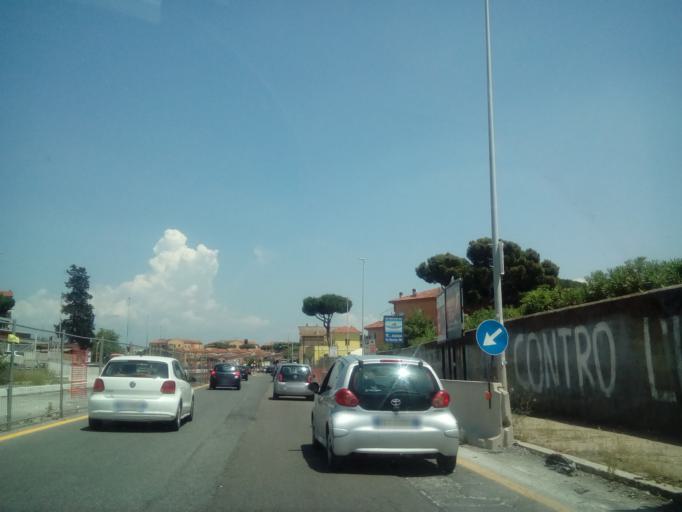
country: IT
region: Latium
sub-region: Citta metropolitana di Roma Capitale
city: Rome
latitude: 41.9240
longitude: 12.5697
